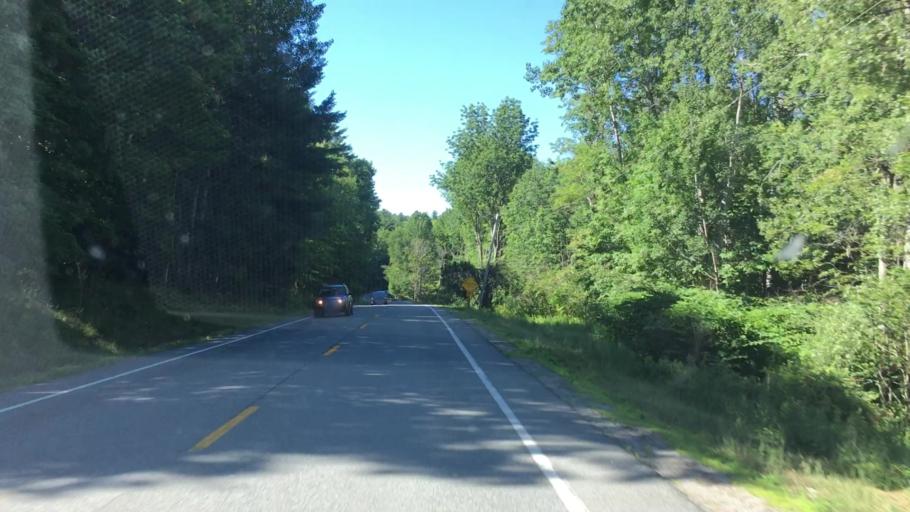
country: US
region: Maine
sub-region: Hancock County
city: Dedham
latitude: 44.6663
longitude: -68.6745
